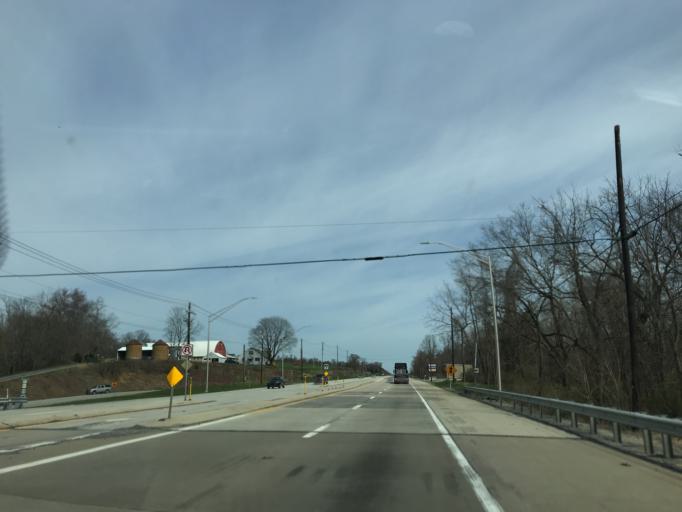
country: US
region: Pennsylvania
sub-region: Dauphin County
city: Millersburg
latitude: 40.5262
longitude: -76.9859
